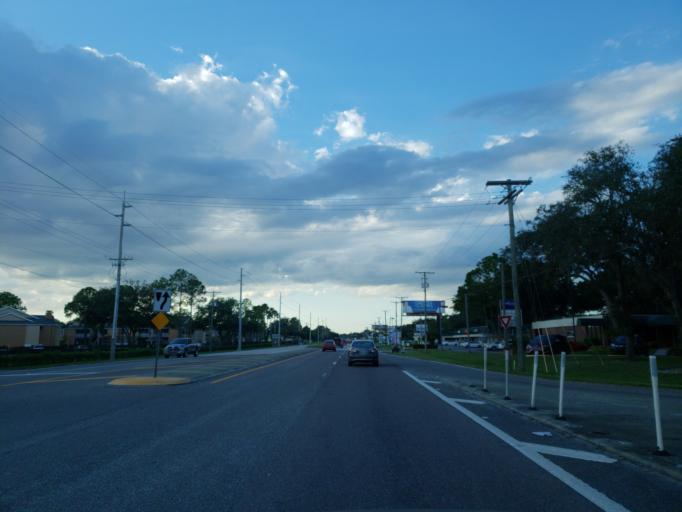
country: US
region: Florida
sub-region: Hillsborough County
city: Carrollwood
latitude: 28.0438
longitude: -82.5133
